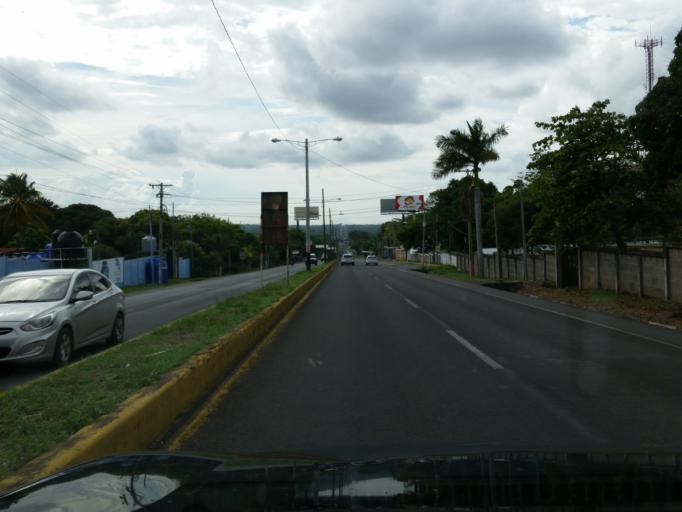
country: NI
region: Masaya
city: Ticuantepe
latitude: 12.0372
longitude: -86.1861
